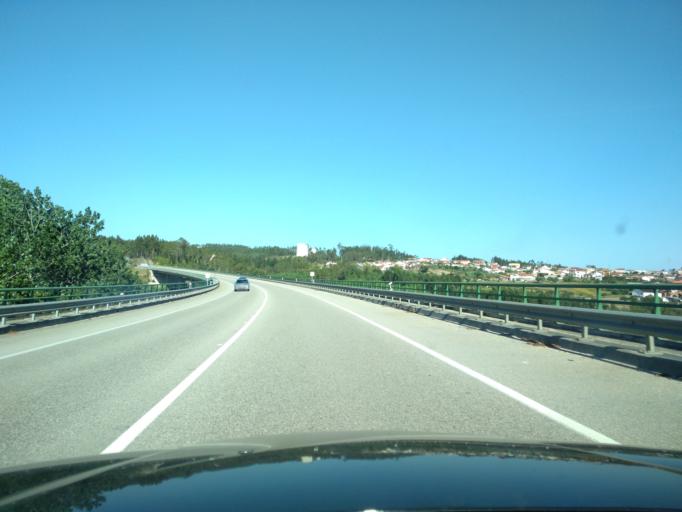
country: PT
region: Leiria
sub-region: Pombal
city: Lourical
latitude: 39.9876
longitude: -8.7363
